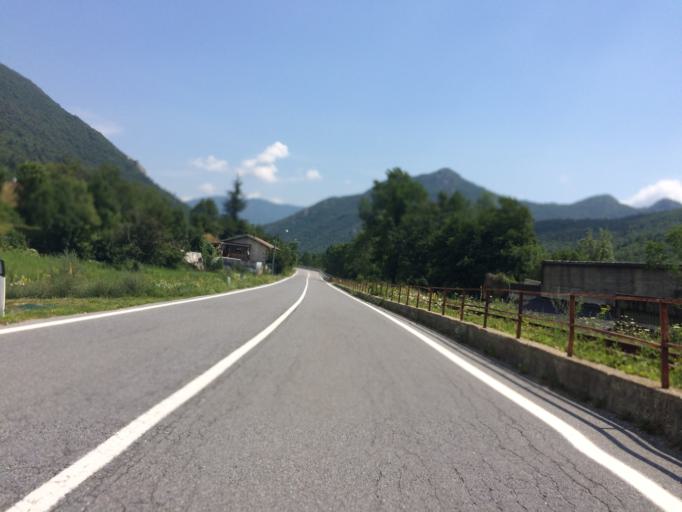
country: IT
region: Piedmont
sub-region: Provincia di Cuneo
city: Garessio
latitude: 44.1837
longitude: 7.9905
